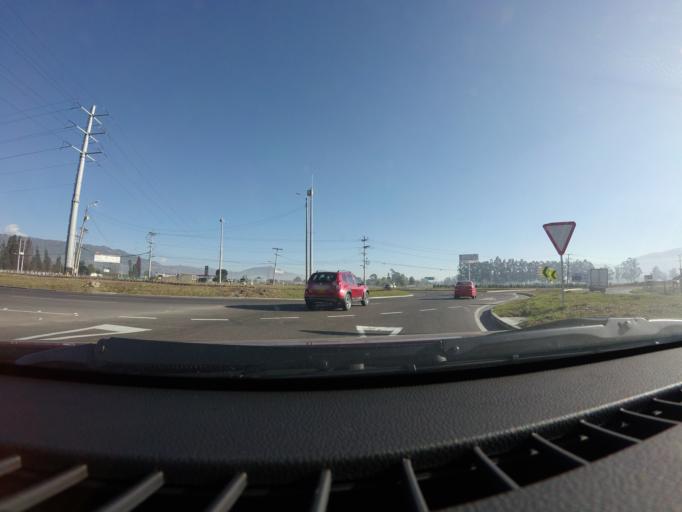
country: CO
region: Cundinamarca
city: Zipaquira
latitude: 5.0098
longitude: -73.9867
